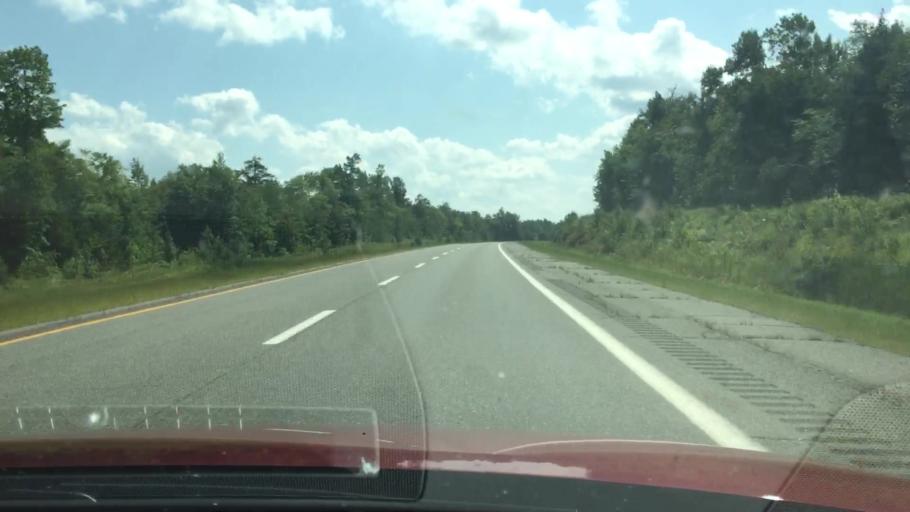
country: US
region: Maine
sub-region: Penobscot County
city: Lincoln
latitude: 45.4309
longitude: -68.5894
